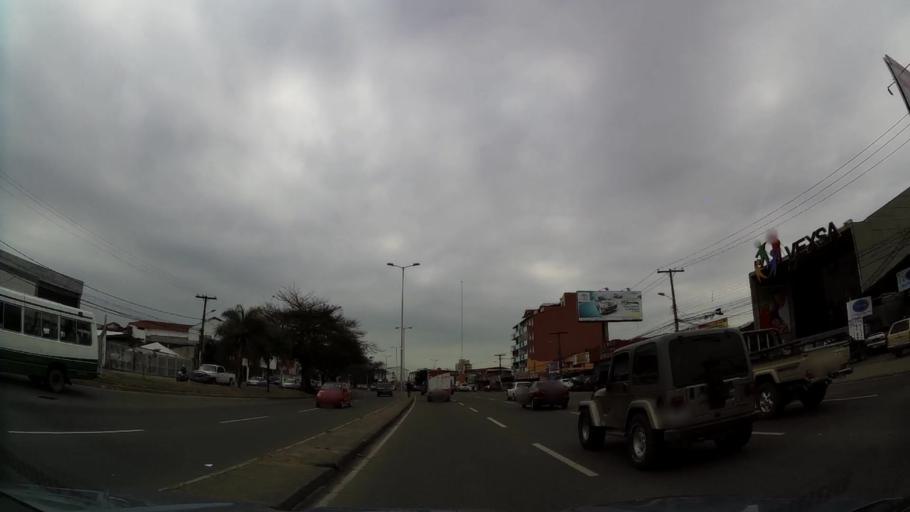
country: BO
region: Santa Cruz
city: Santa Cruz de la Sierra
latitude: -17.7745
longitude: -63.1688
